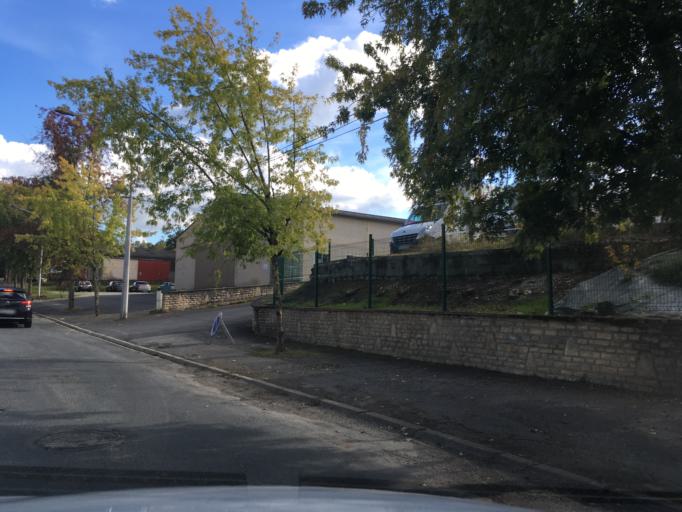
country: FR
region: Limousin
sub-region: Departement de la Correze
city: Malemort-sur-Correze
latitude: 45.1522
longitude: 1.5613
